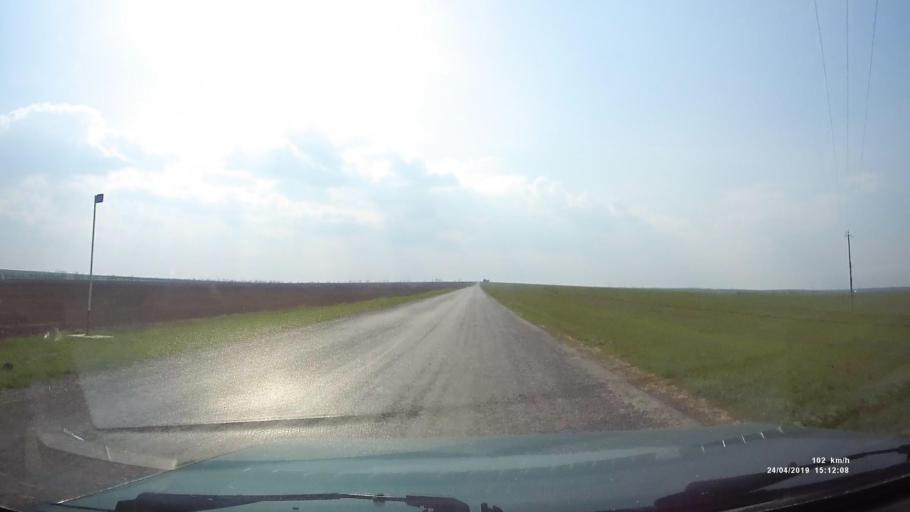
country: RU
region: Rostov
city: Remontnoye
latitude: 46.5464
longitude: 43.3071
